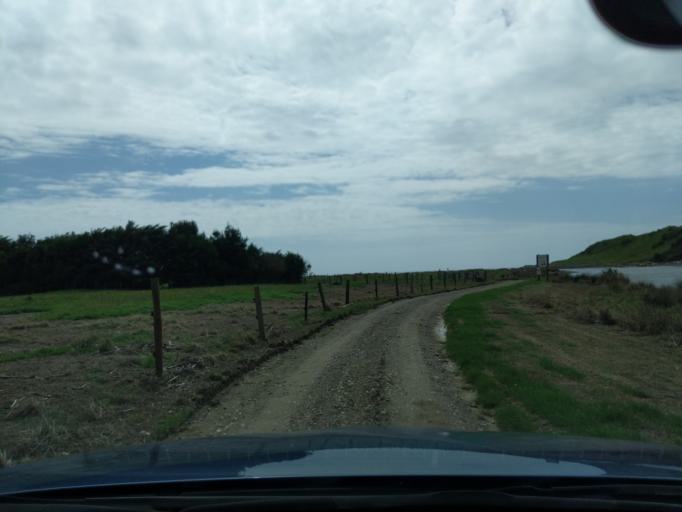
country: NZ
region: Tasman
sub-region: Tasman District
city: Takaka
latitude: -40.6437
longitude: 172.4318
